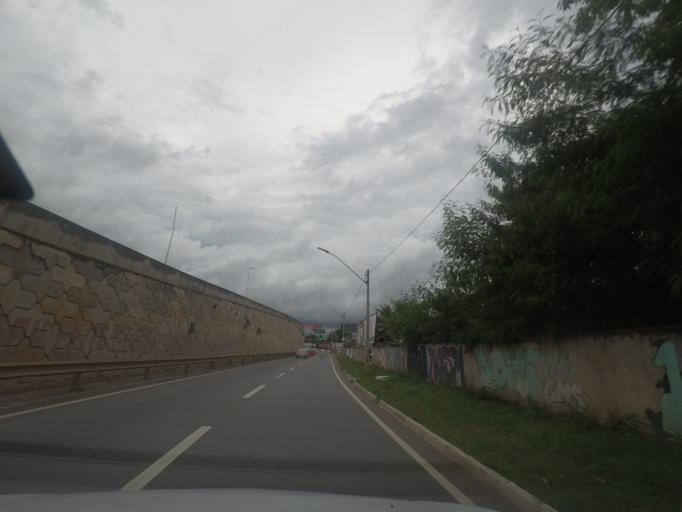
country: BR
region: Goias
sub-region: Goiania
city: Goiania
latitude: -16.6930
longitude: -49.2441
